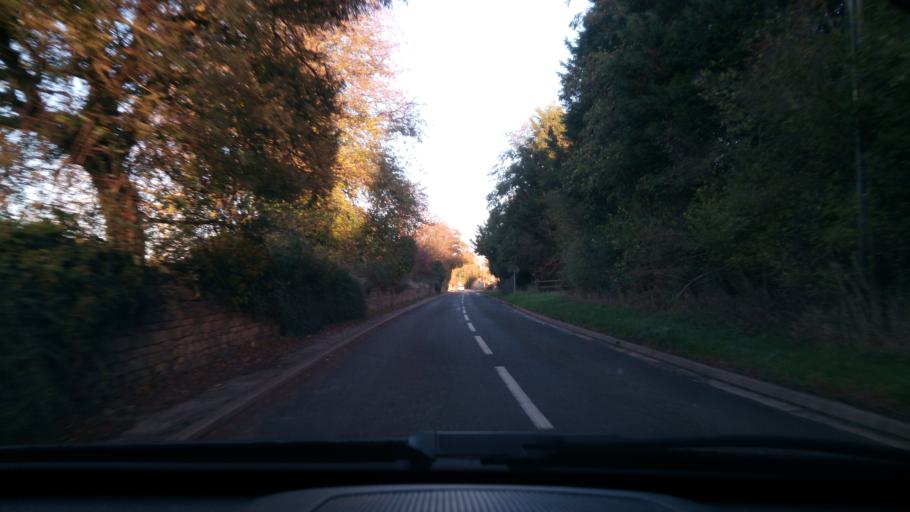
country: GB
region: England
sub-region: Peterborough
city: Ufford
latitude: 52.6397
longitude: -0.3893
